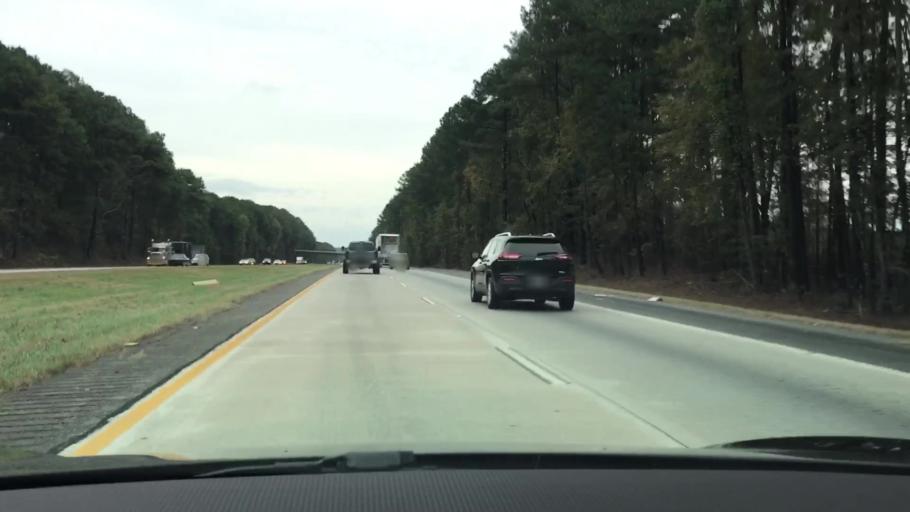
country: US
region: Georgia
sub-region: Greene County
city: Greensboro
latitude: 33.5473
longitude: -83.1747
